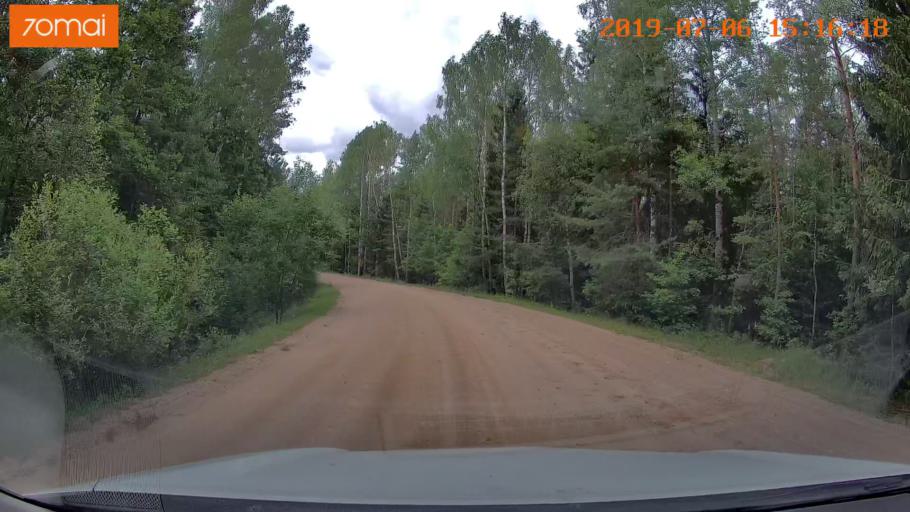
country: BY
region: Minsk
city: Ivyanyets
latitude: 53.9802
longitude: 26.6799
